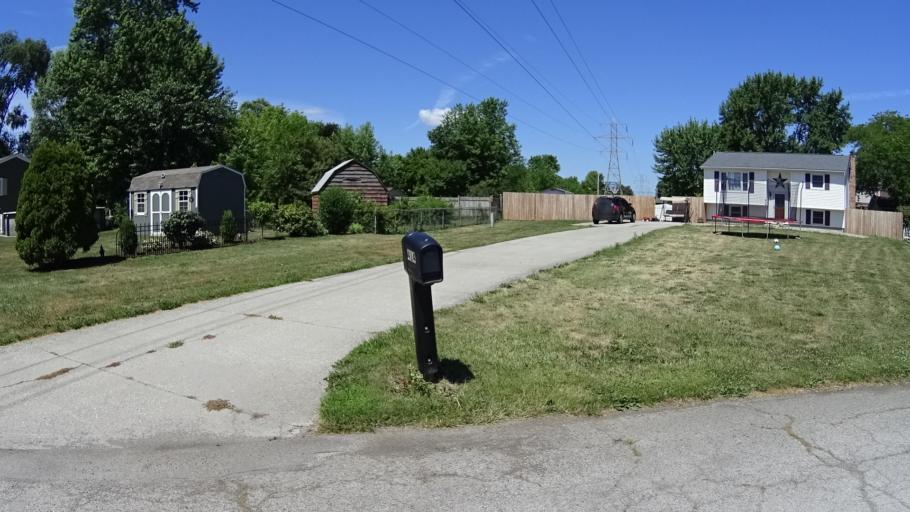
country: US
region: Ohio
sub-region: Erie County
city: Sandusky
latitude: 41.4100
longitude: -82.6895
